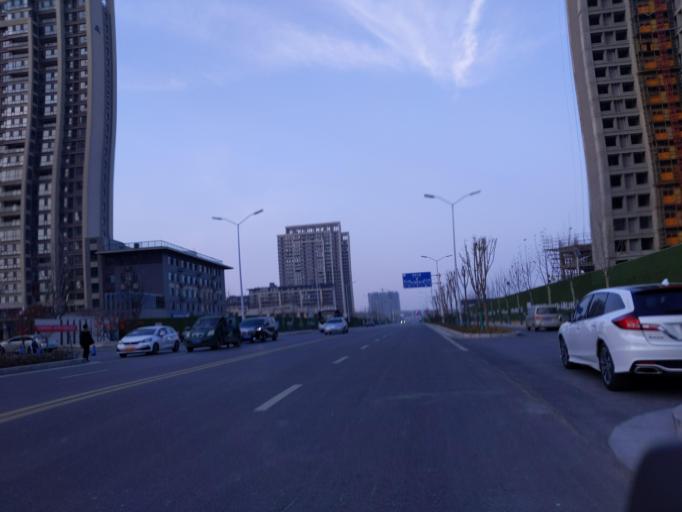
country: CN
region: Henan Sheng
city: Puyang
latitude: 35.8052
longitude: 115.0112
